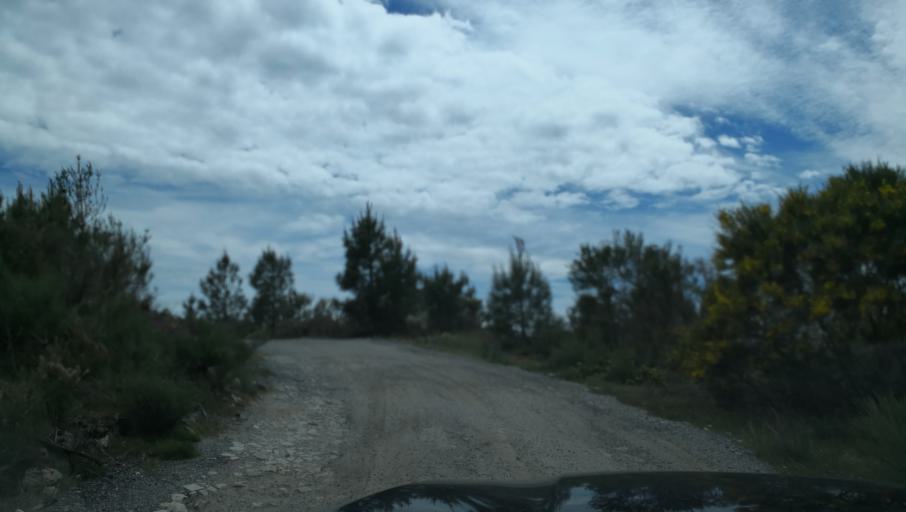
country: PT
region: Vila Real
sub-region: Vila Real
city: Vila Real
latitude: 41.3644
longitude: -7.7017
